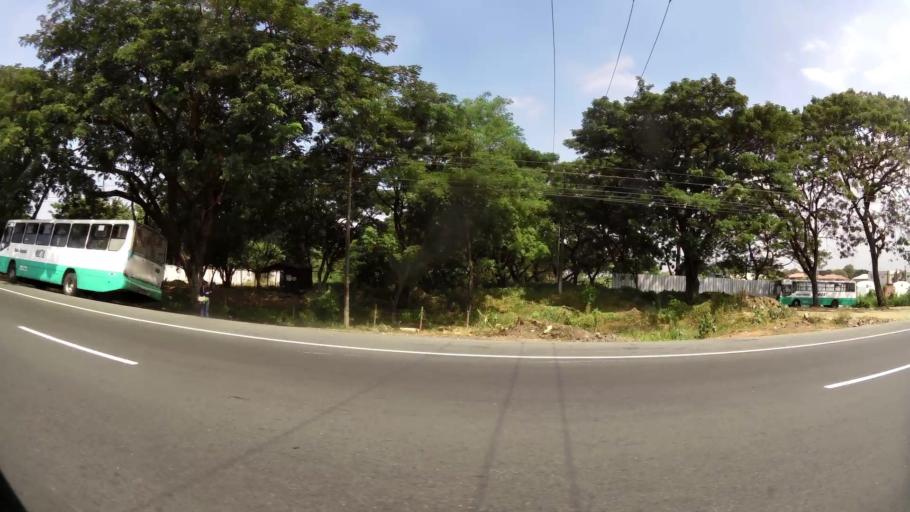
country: EC
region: Guayas
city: Eloy Alfaro
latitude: -2.0517
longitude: -79.8932
